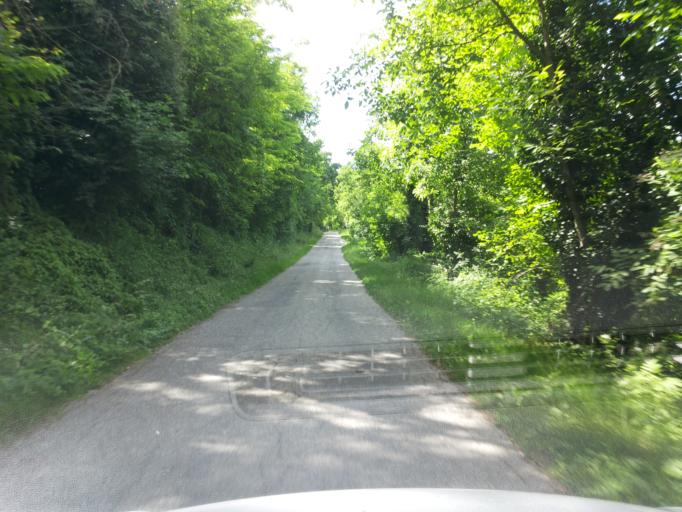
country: IT
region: Piedmont
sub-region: Provincia di Alessandria
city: Serralunga di Crea
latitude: 45.1041
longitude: 8.2770
